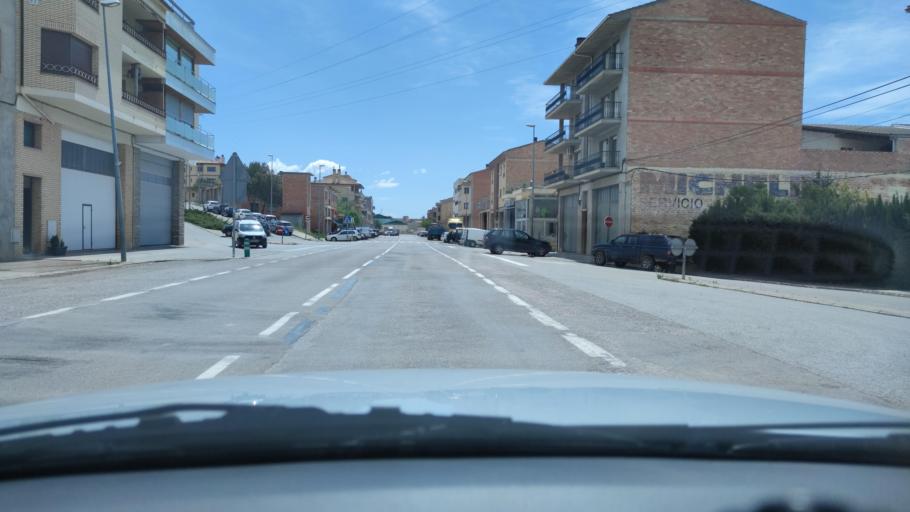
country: ES
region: Catalonia
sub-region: Provincia de Lleida
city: Solsona
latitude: 42.0007
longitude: 1.5184
